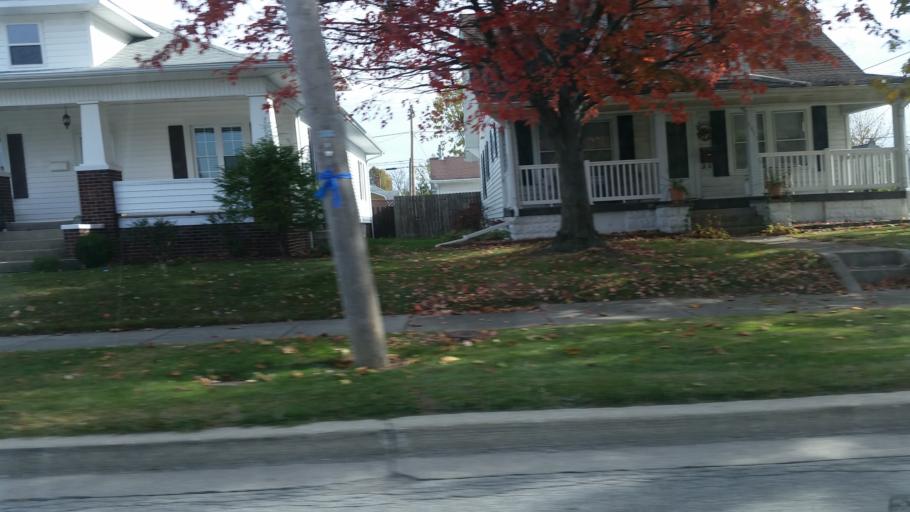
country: US
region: Indiana
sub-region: Howard County
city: Kokomo
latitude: 40.4672
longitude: -86.1337
